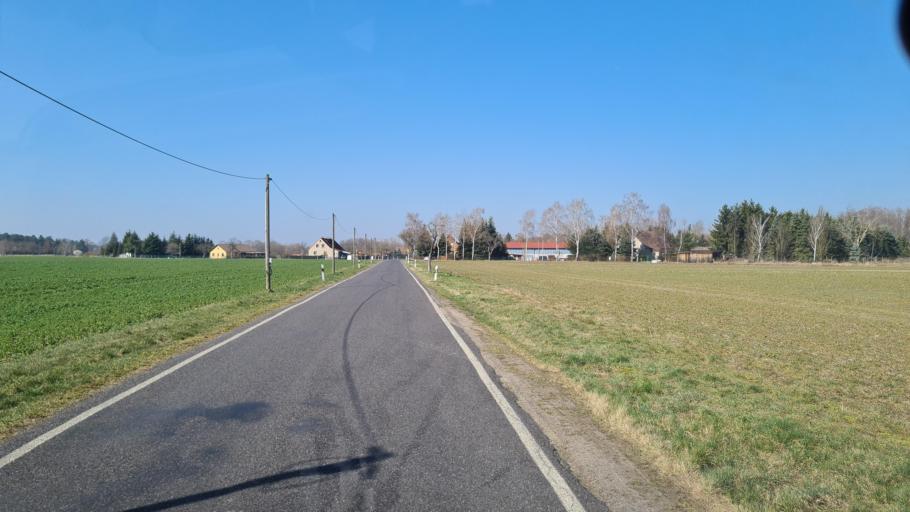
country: DE
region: Brandenburg
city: Vetschau
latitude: 51.7860
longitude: 14.0504
